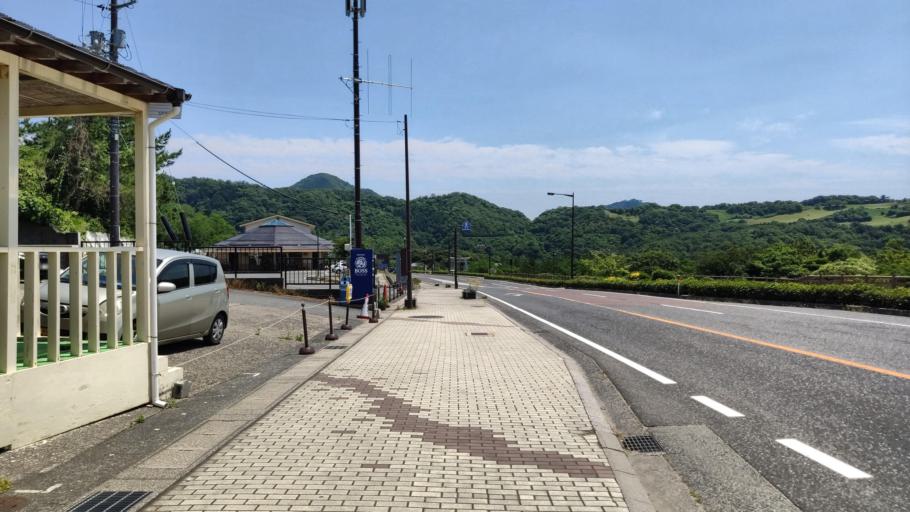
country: JP
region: Tottori
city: Tottori
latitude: 35.5406
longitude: 134.2366
